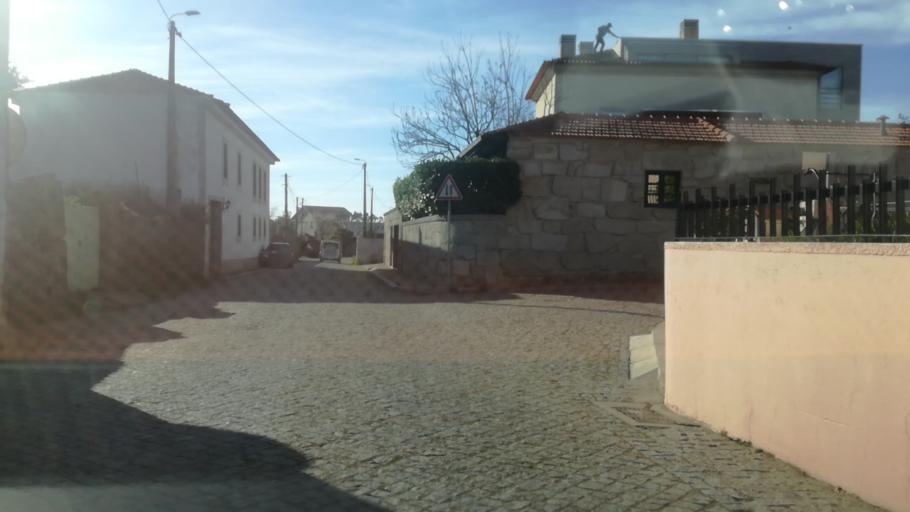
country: PT
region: Porto
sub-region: Matosinhos
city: Santa Cruz do Bispo
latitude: 41.2514
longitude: -8.6729
